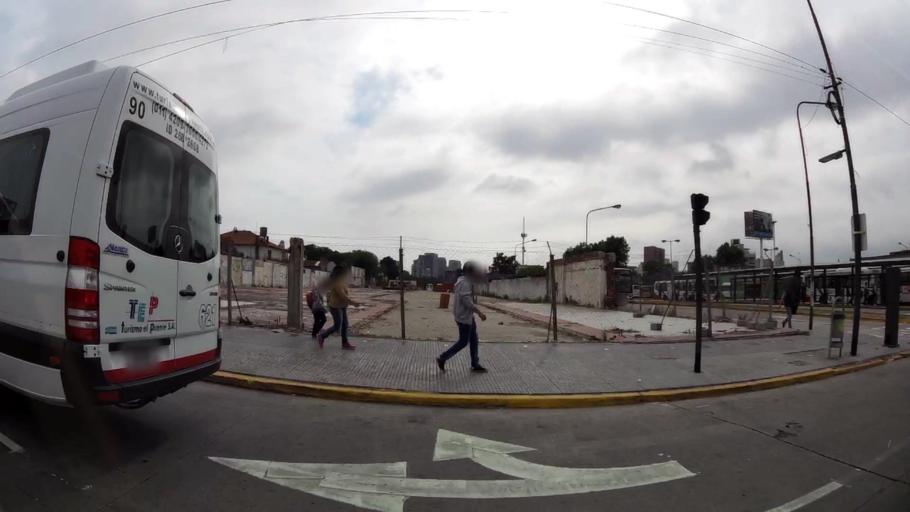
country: AR
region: Buenos Aires
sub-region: Partido de Vicente Lopez
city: Olivos
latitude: -34.5369
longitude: -58.4768
